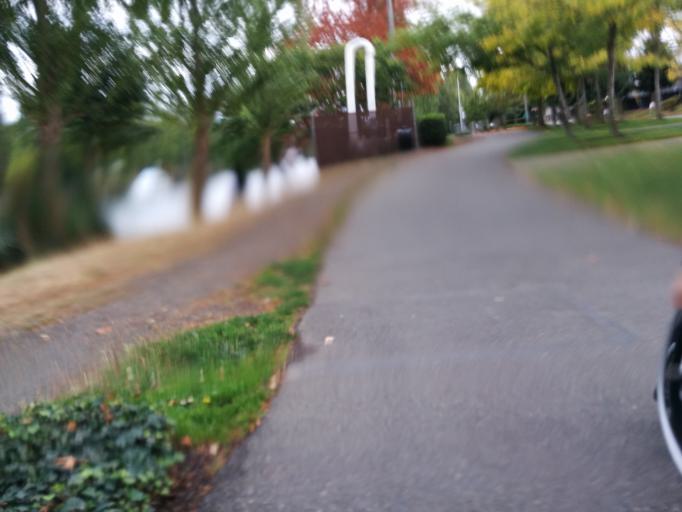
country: US
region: Washington
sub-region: King County
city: Seattle
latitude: 47.6500
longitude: -122.3537
